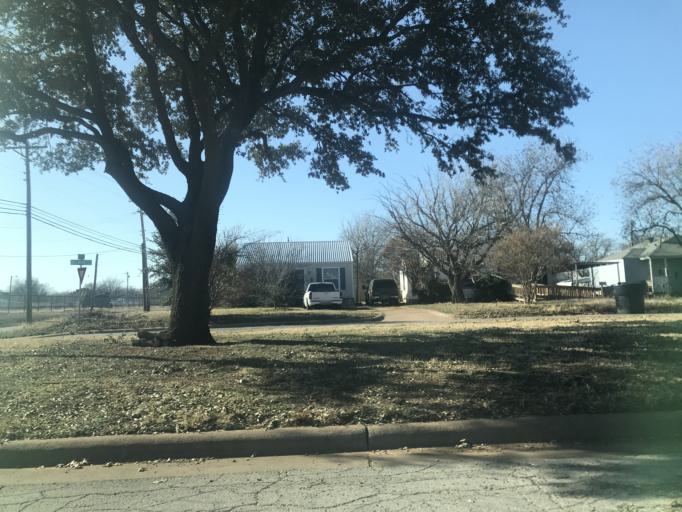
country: US
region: Texas
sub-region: Taylor County
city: Abilene
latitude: 32.4233
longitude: -99.7373
